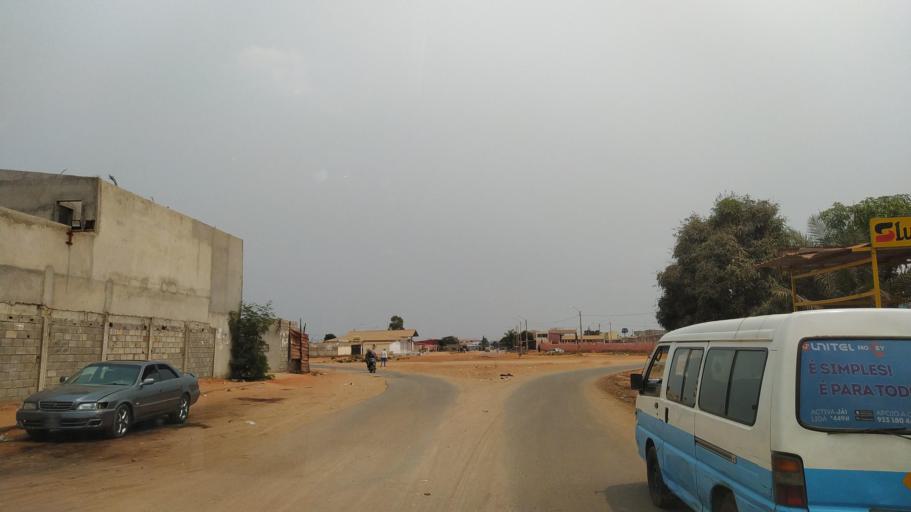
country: AO
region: Luanda
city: Luanda
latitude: -9.0702
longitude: 13.4153
